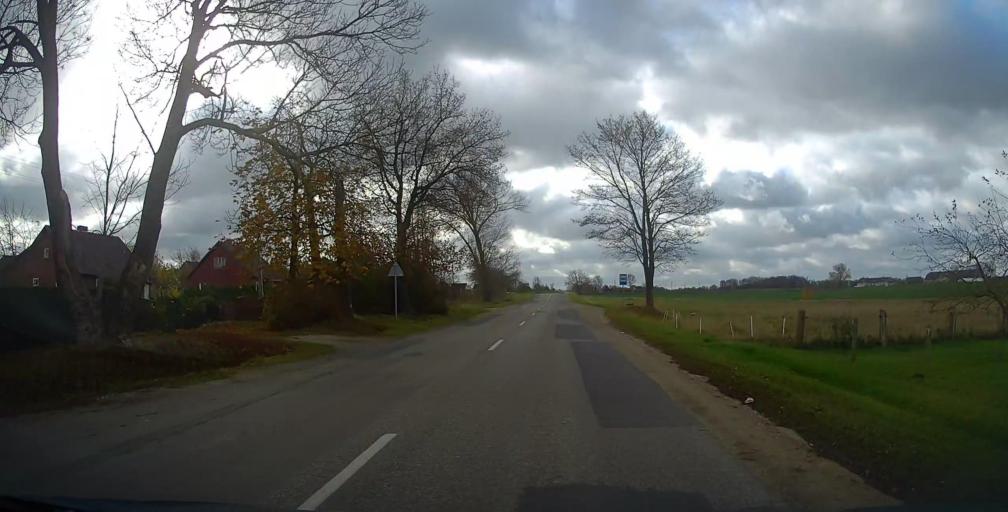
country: LT
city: Kybartai
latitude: 54.6102
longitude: 22.7442
